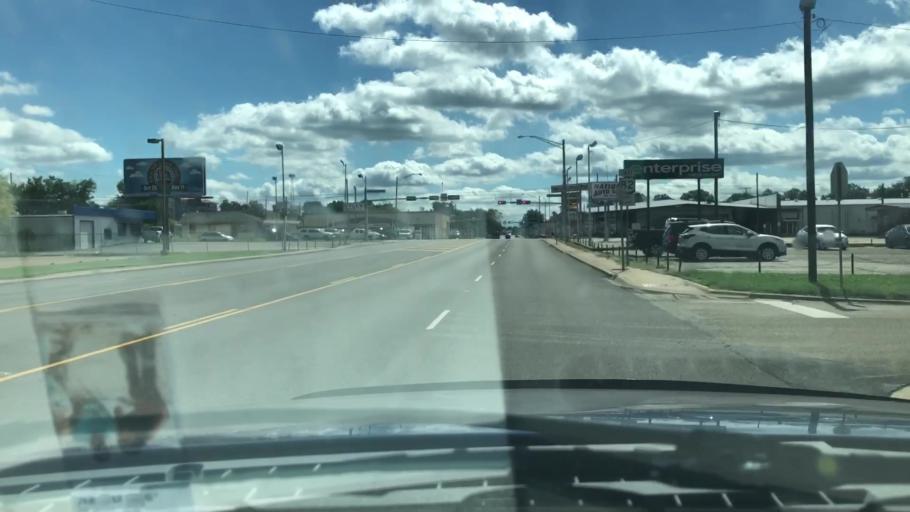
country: US
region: Texas
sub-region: Bowie County
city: Texarkana
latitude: 33.4271
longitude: -94.0492
